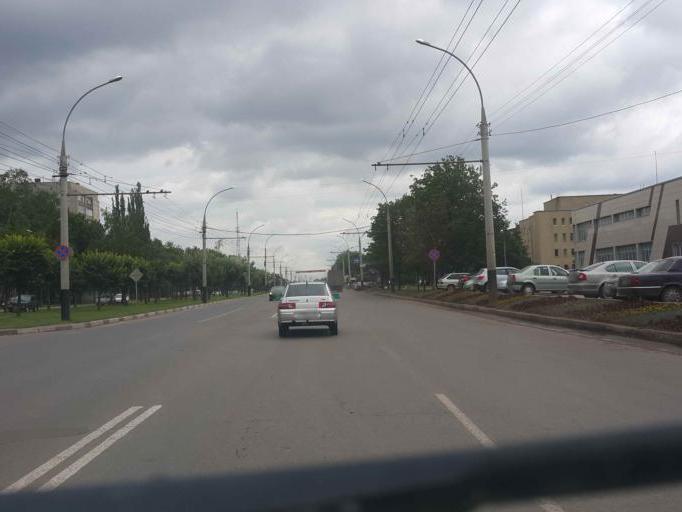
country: RU
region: Tambov
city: Tambov
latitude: 52.7550
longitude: 41.4094
